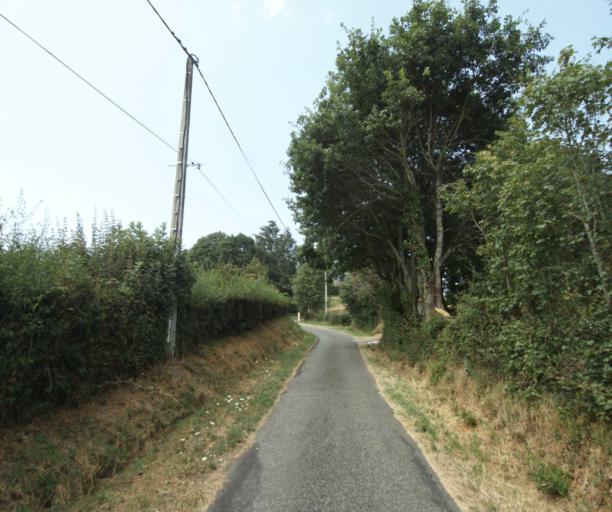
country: FR
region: Bourgogne
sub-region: Departement de Saone-et-Loire
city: Gueugnon
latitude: 46.6056
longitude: 4.0360
